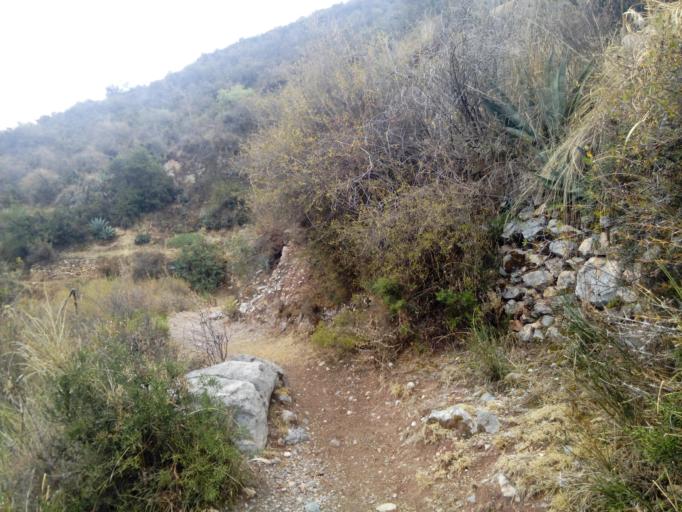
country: PE
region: Ayacucho
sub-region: Provincia de Victor Fajardo
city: Canaria
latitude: -13.9014
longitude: -73.9325
